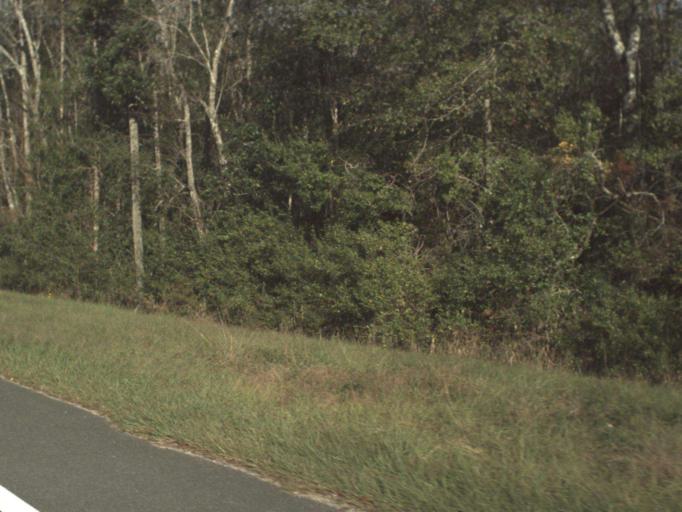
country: US
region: Florida
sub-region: Washington County
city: Chipley
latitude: 30.7404
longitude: -85.6038
